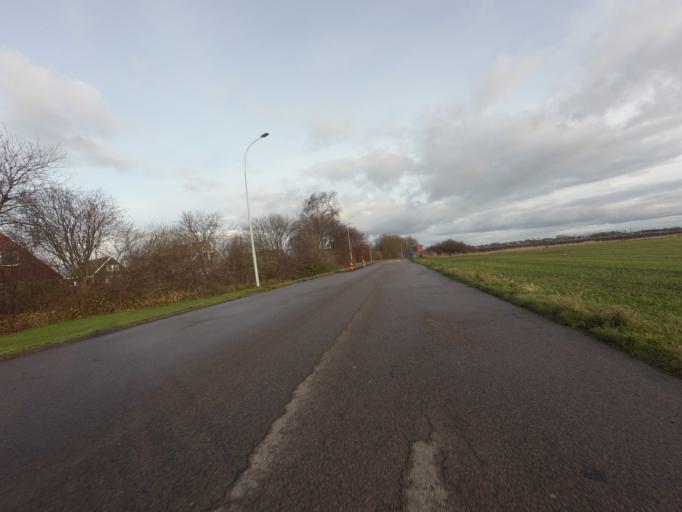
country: SE
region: Skane
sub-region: Hoganas Kommun
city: Hoganas
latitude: 56.1896
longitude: 12.5849
